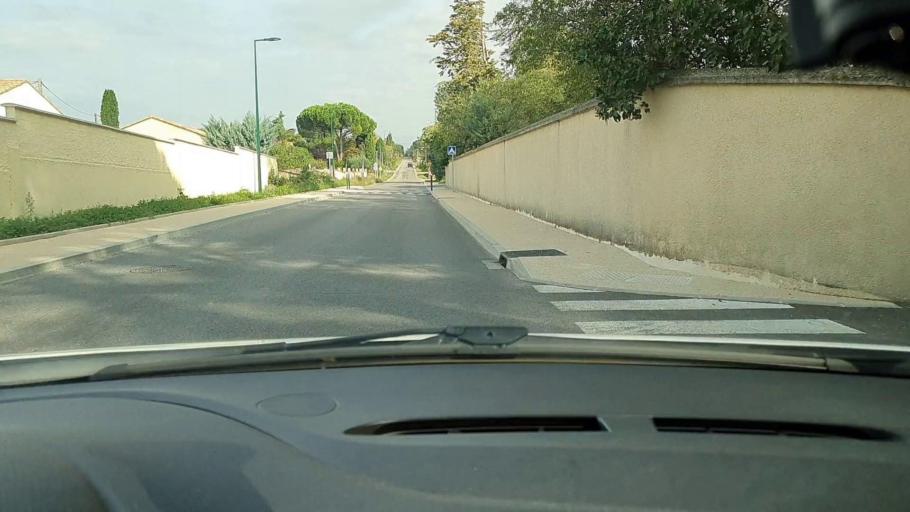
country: FR
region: Languedoc-Roussillon
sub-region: Departement du Gard
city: Saint-Quentin-la-Poterie
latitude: 44.1063
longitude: 4.4567
